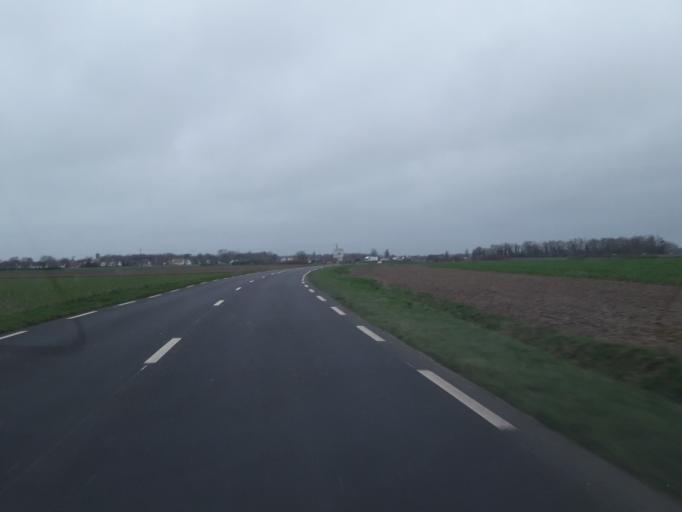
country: FR
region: Ile-de-France
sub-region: Departement de l'Essonne
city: Leudeville
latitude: 48.5641
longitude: 2.3430
